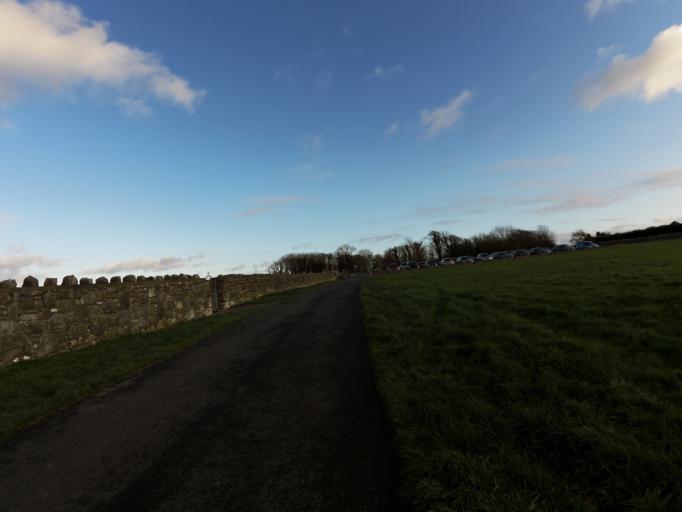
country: IE
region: Connaught
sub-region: County Galway
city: Oranmore
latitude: 53.2464
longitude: -8.9573
